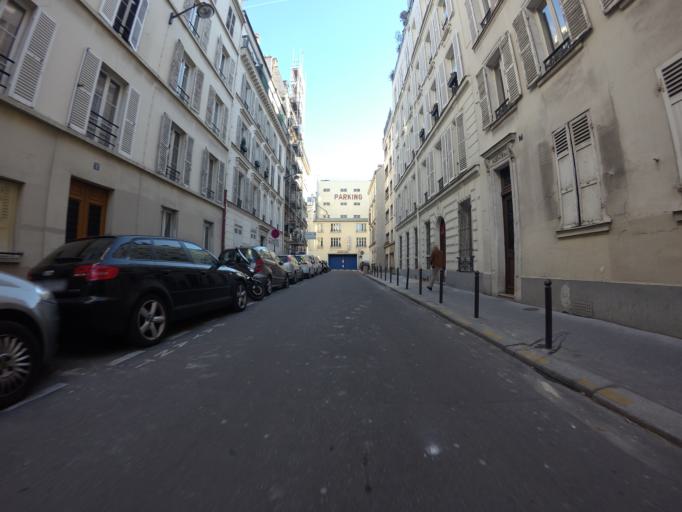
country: FR
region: Ile-de-France
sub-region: Departement des Hauts-de-Seine
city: Clichy
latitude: 48.8837
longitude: 2.3153
